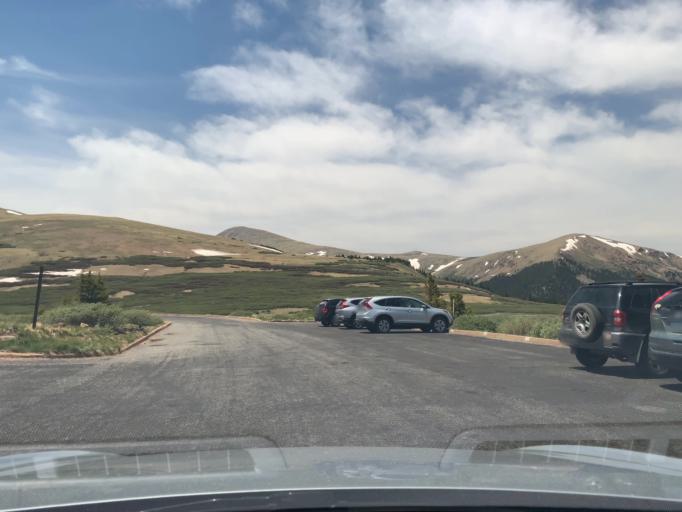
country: US
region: Colorado
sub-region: Clear Creek County
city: Georgetown
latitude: 39.5973
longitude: -105.7125
